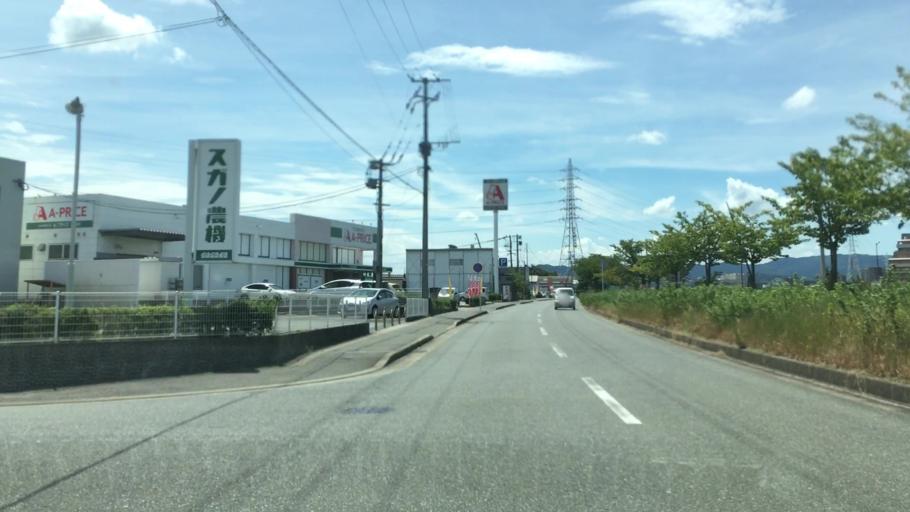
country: JP
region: Fukuoka
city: Onojo
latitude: 33.5417
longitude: 130.4830
